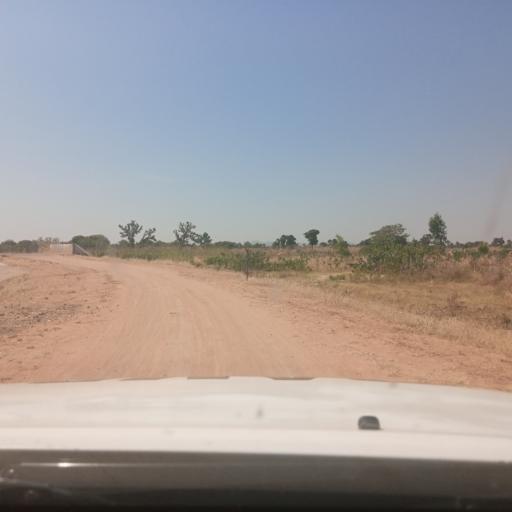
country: NG
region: Adamawa
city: Little Gombi
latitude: 9.7786
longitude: 12.5829
